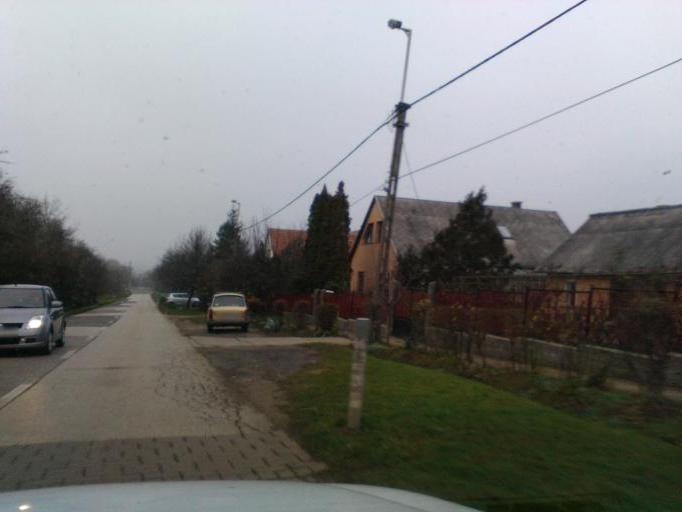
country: HU
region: Pest
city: Toeroekbalint
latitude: 47.4450
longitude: 18.8982
